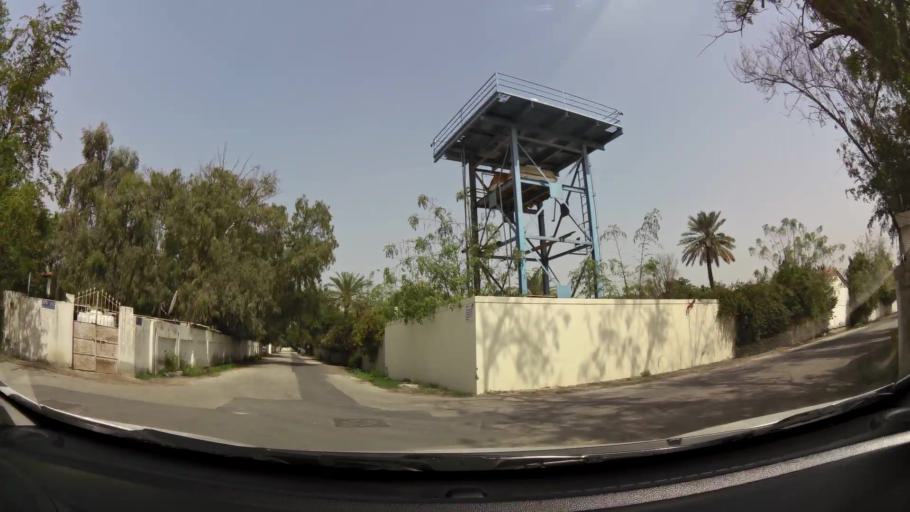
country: BH
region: Manama
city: Jidd Hafs
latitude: 26.2257
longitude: 50.5026
